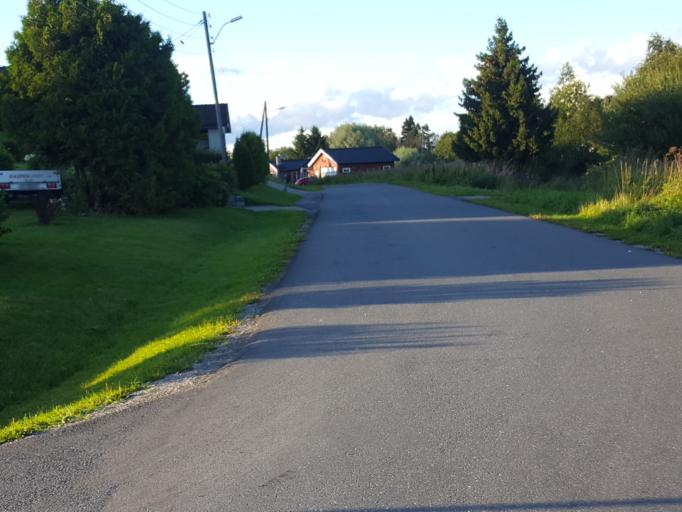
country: NO
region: Akershus
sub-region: Ski
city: Ski
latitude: 59.6803
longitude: 10.8883
